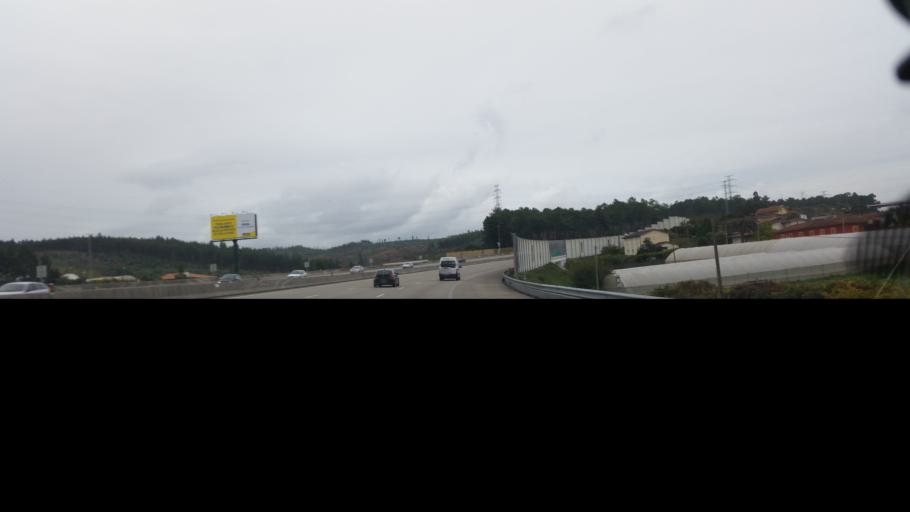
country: PT
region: Porto
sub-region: Trofa
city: Sao Romao do Coronado
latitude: 41.3015
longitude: -8.5378
